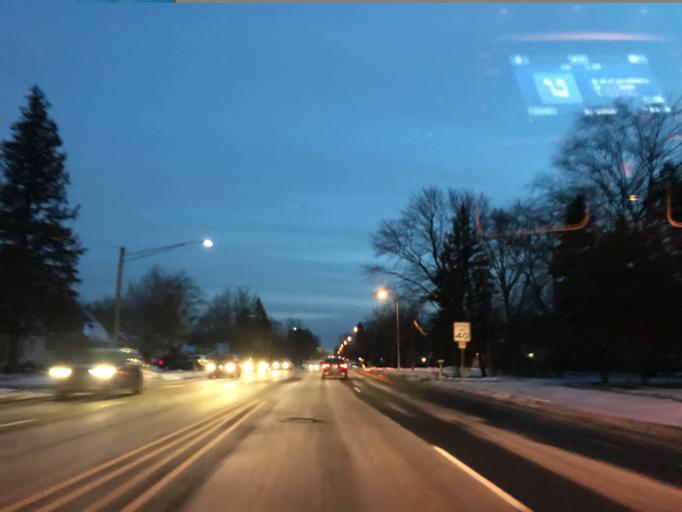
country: US
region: Michigan
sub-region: Wayne County
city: Redford
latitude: 42.4263
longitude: -83.3162
